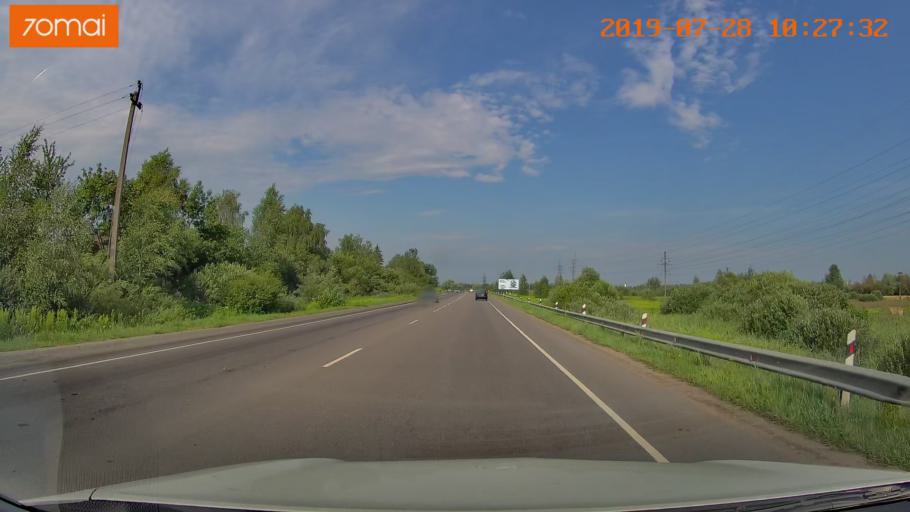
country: RU
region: Kaliningrad
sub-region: Gorod Kaliningrad
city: Kaliningrad
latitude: 54.7709
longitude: 20.5161
